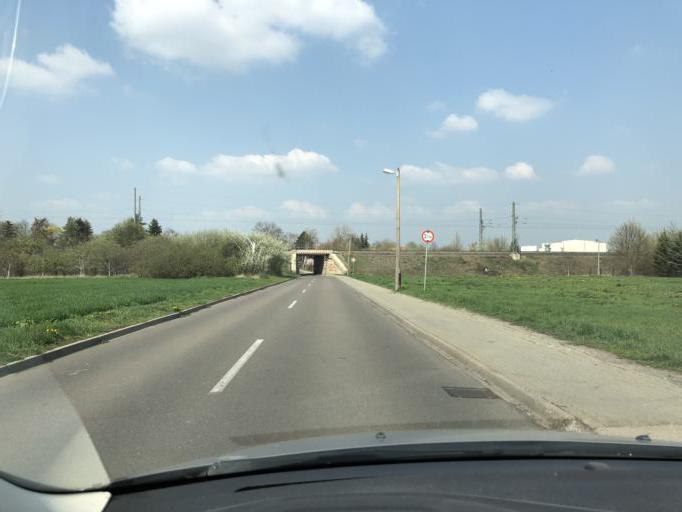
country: DE
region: Saxony-Anhalt
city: Landsberg
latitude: 51.5262
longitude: 12.1536
